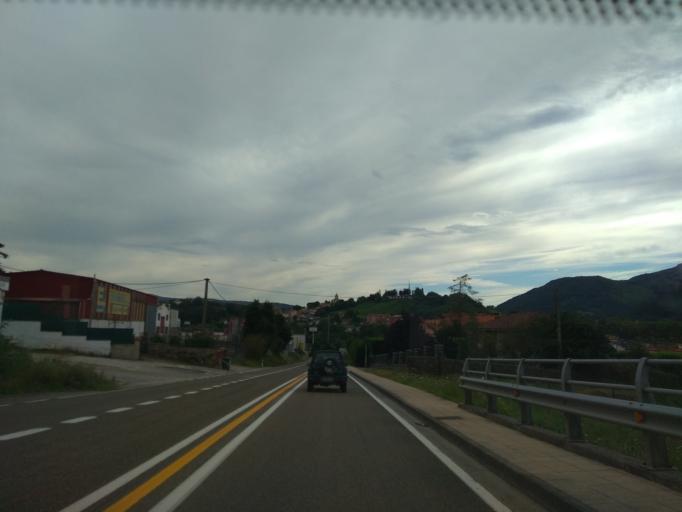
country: ES
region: Cantabria
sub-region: Provincia de Cantabria
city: Entrambasaguas
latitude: 43.3875
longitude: -3.7256
